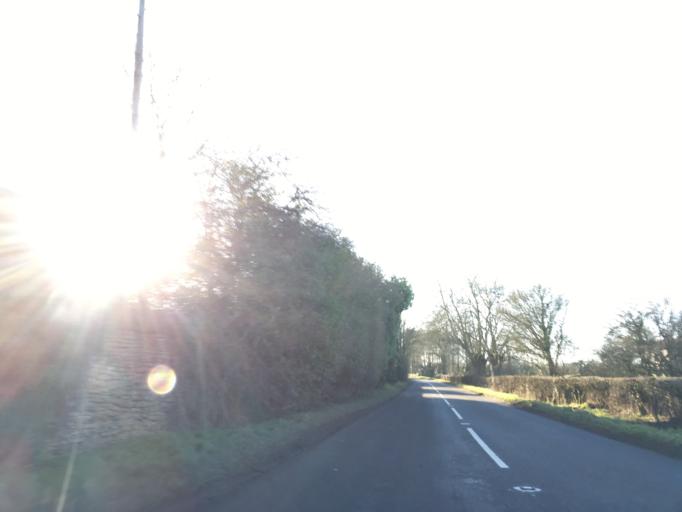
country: GB
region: England
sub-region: Wiltshire
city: Luckington
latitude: 51.5472
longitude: -2.2453
